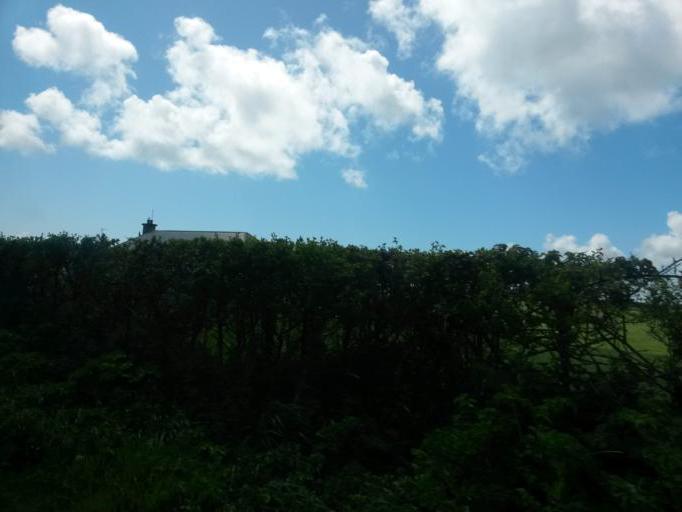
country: IE
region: Munster
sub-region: Waterford
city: Dunmore East
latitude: 52.1834
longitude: -6.8948
